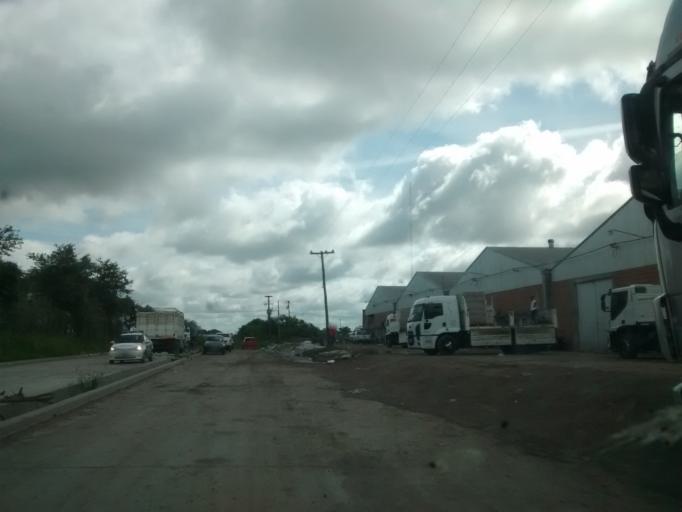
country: AR
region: Chaco
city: Fontana
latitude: -27.4070
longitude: -58.9806
